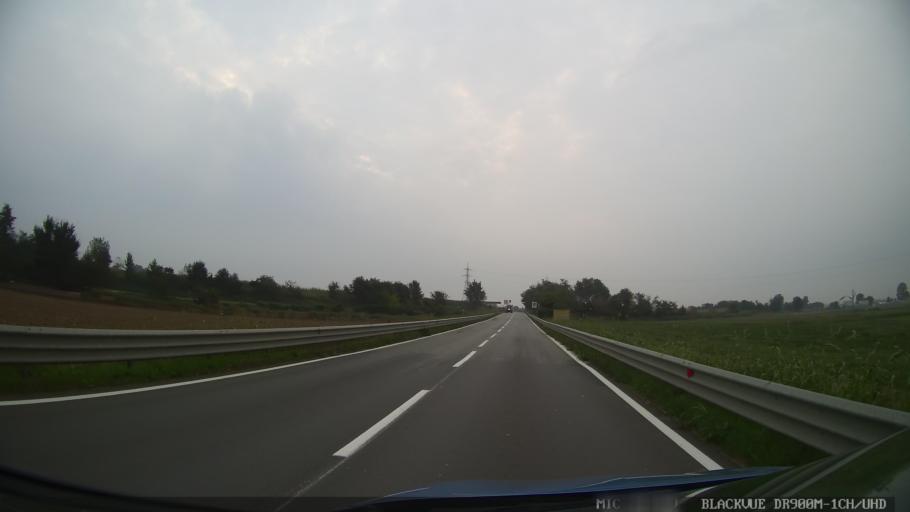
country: IT
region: Piedmont
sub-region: Provincia di Torino
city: Carmagnola
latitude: 44.8733
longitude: 7.7046
